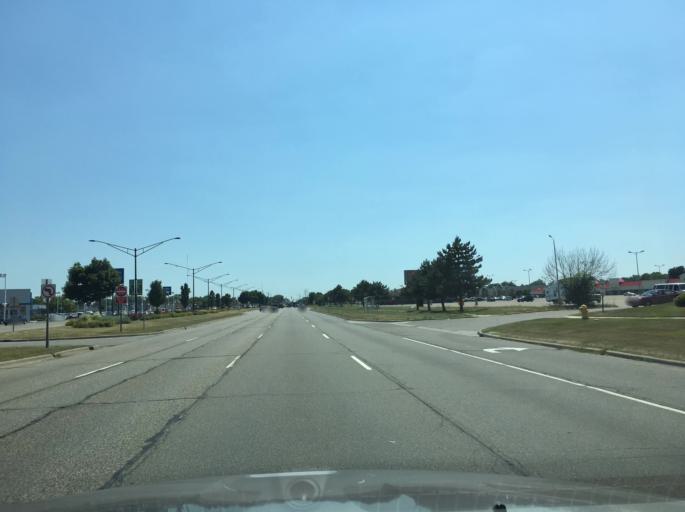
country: US
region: Michigan
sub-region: Macomb County
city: Clinton
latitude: 42.5593
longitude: -82.8974
